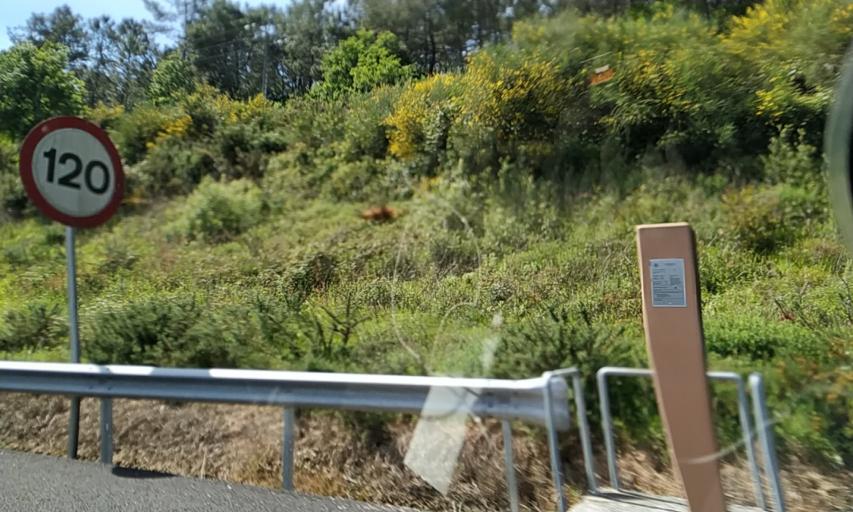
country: ES
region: Galicia
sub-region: Provincia de Pontevedra
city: Caldas de Reis
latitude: 42.6402
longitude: -8.6555
